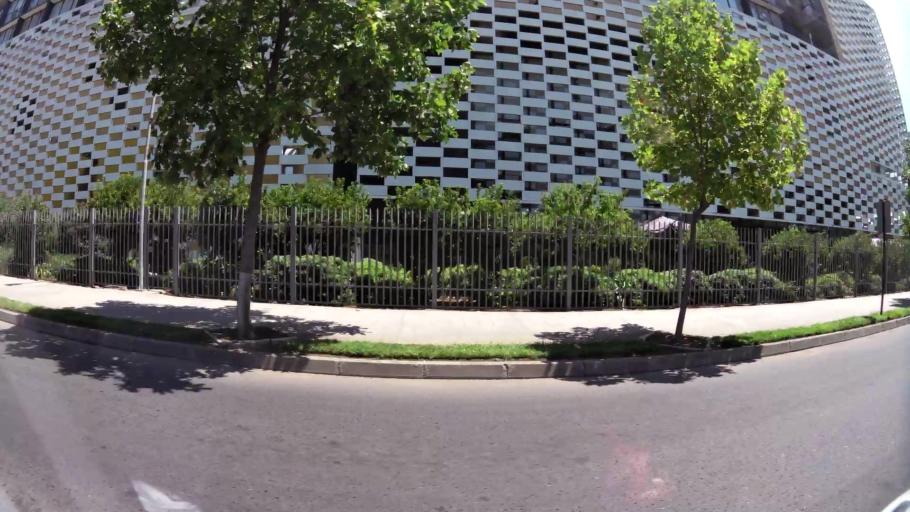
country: CL
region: Maule
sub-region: Provincia de Talca
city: Talca
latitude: -35.4337
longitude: -71.6294
